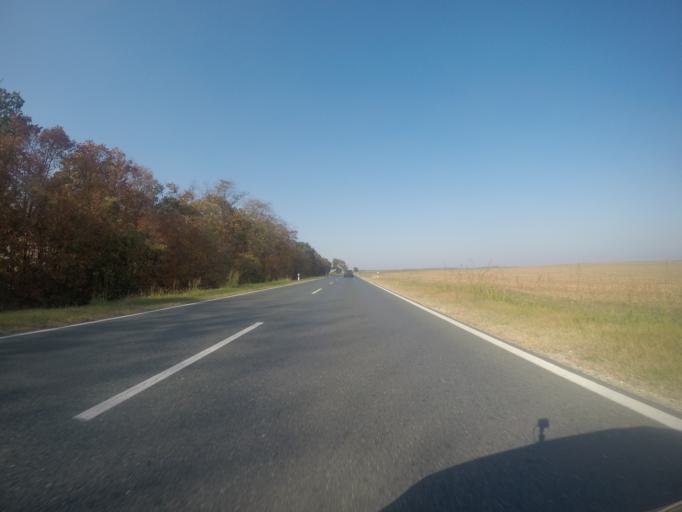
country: HU
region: Tolna
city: Madocsa
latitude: 46.7097
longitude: 18.8878
